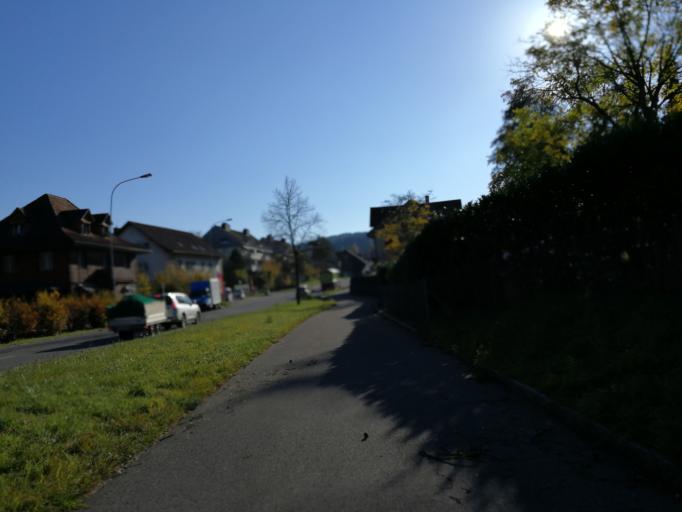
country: CH
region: Zurich
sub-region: Bezirk Uster
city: Esslingen
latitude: 47.2904
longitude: 8.7130
